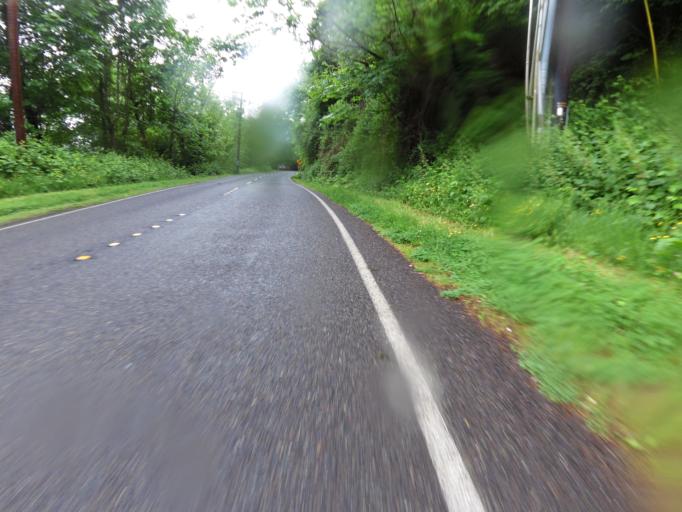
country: US
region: Washington
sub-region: King County
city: Bryn Mawr-Skyway
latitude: 47.5278
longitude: -122.2262
